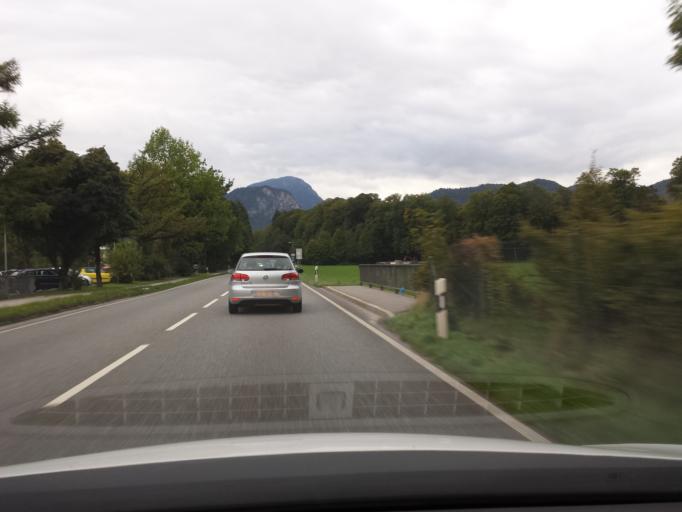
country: DE
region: Bavaria
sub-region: Upper Bavaria
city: Bad Reichenhall
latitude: 47.7325
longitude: 12.8743
